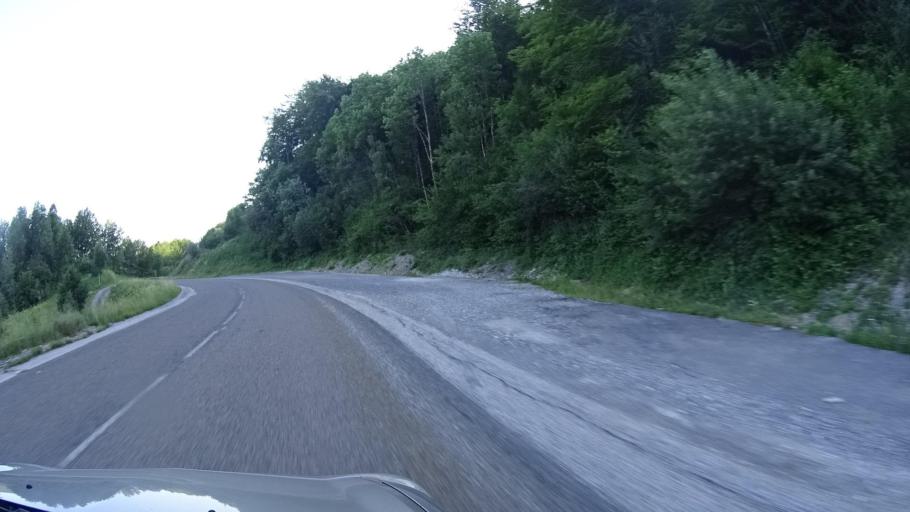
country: FR
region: Franche-Comte
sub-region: Departement du Jura
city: Longchaumois
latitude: 46.5140
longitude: 5.9594
